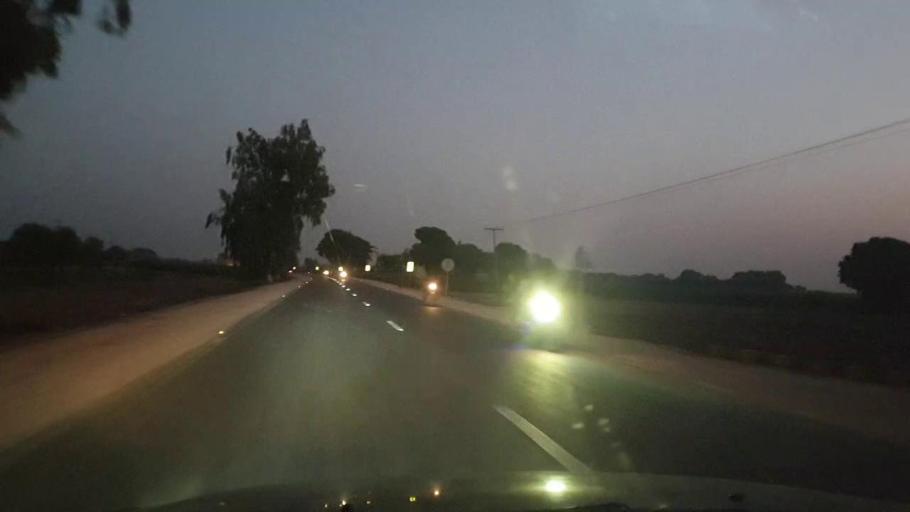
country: PK
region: Sindh
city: Tando Allahyar
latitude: 25.3863
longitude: 68.7720
